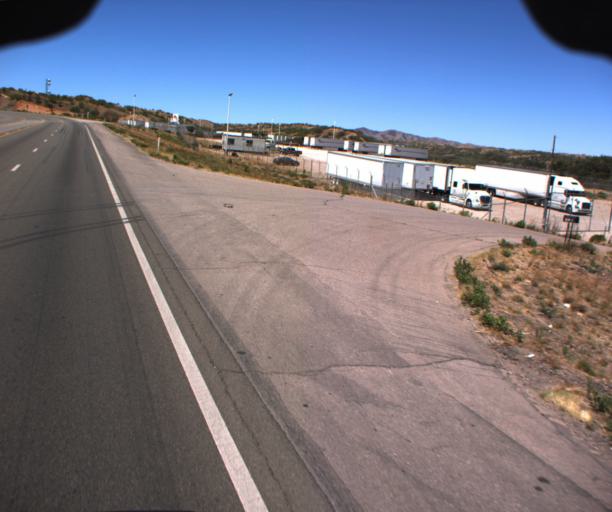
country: US
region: Arizona
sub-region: Santa Cruz County
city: Nogales
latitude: 31.3509
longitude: -110.9619
